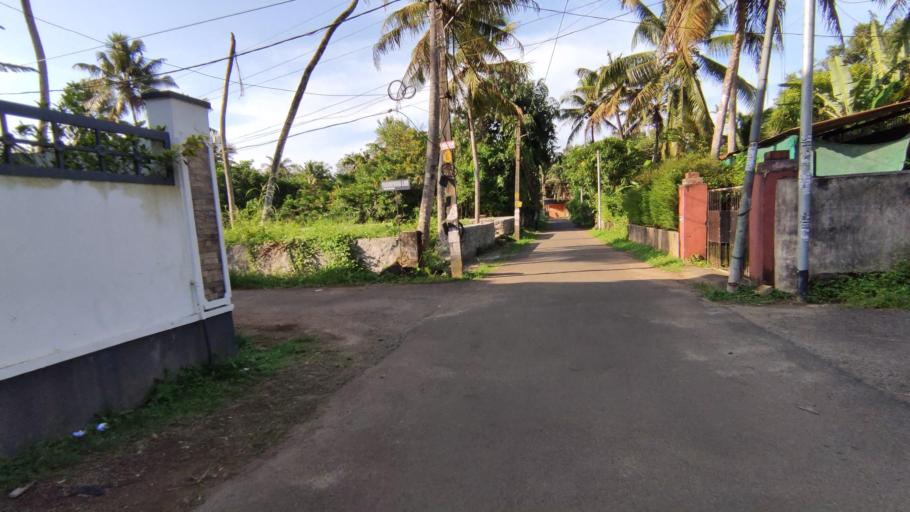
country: IN
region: Kerala
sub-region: Kottayam
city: Kottayam
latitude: 9.5974
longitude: 76.5118
